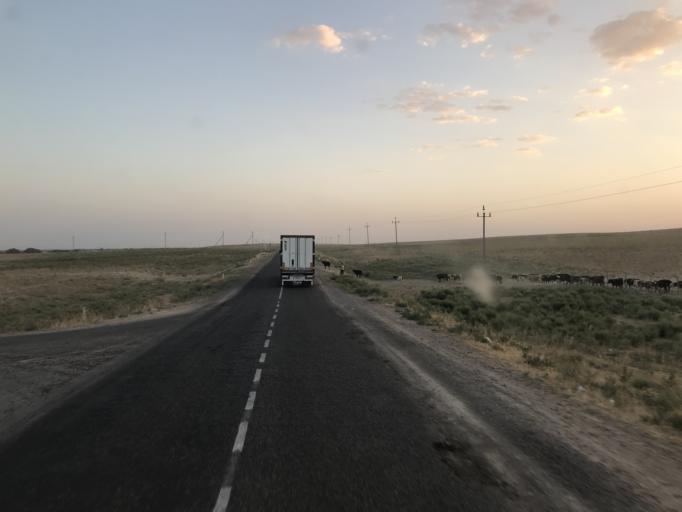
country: UZ
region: Toshkent
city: Amir Timur
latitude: 41.3495
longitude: 68.7093
